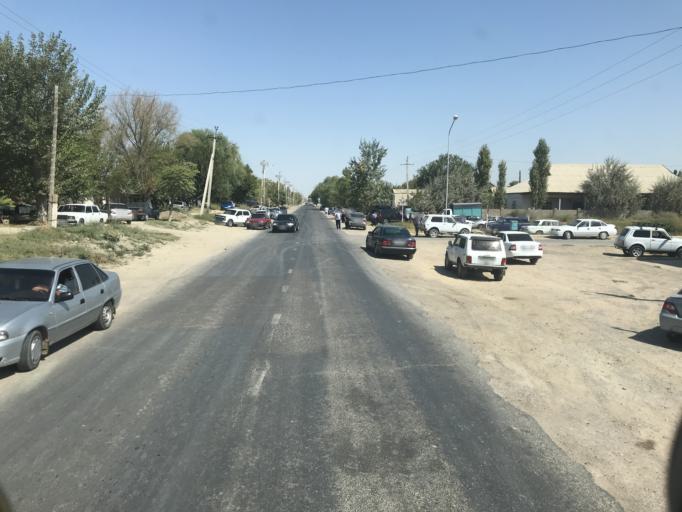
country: KZ
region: Ongtustik Qazaqstan
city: Ilyich
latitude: 40.9324
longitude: 68.4883
